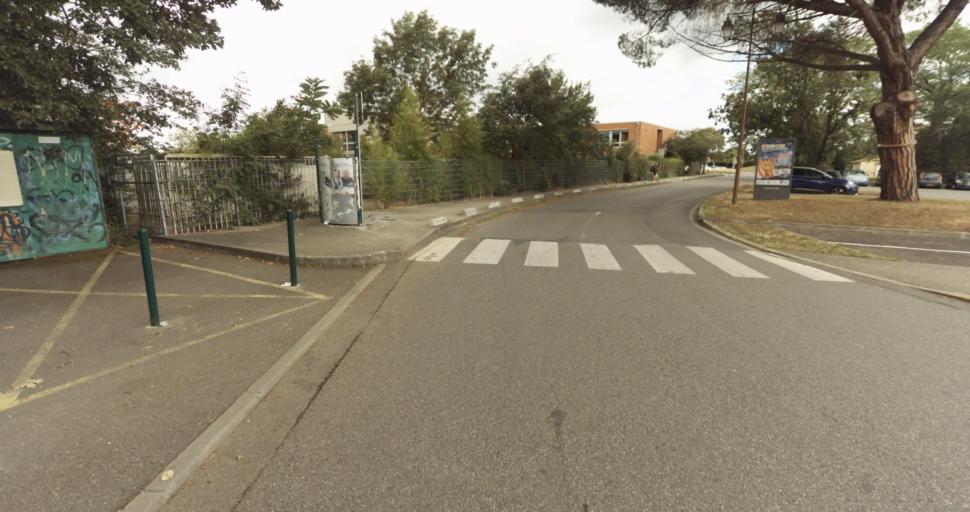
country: FR
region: Midi-Pyrenees
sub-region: Departement de la Haute-Garonne
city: Fonsorbes
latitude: 43.5513
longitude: 1.2339
